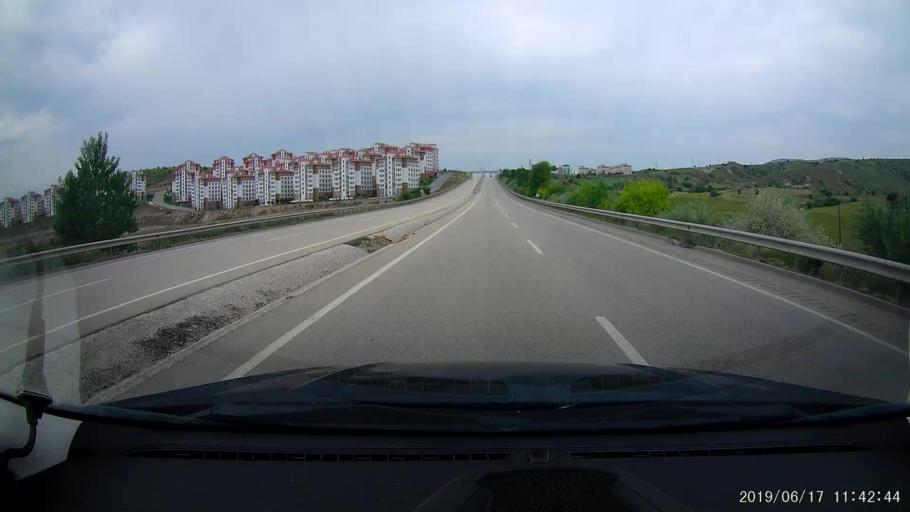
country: TR
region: Cankiri
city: Kursunlu
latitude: 40.8376
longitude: 33.2938
